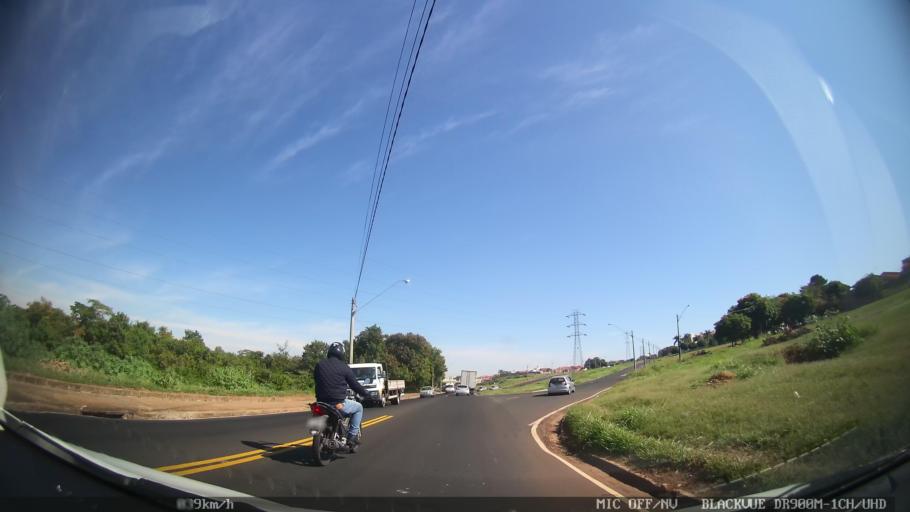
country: BR
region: Sao Paulo
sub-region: Sao Jose Do Rio Preto
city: Sao Jose do Rio Preto
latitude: -20.8031
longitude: -49.4126
